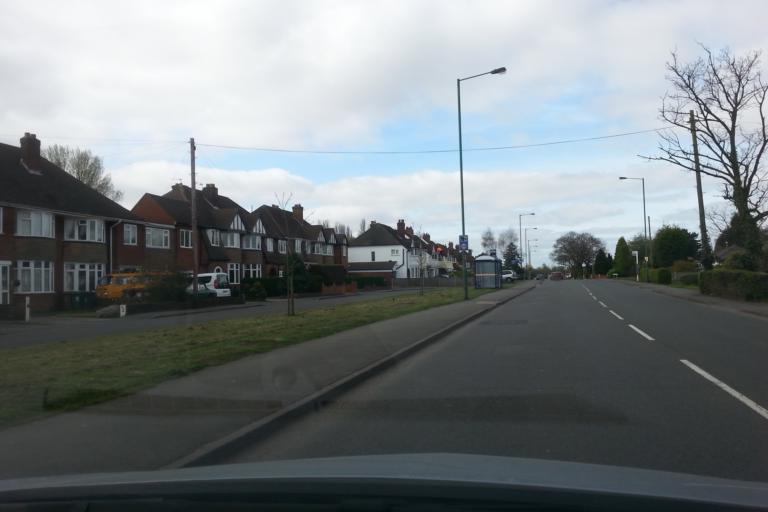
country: GB
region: England
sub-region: Walsall
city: Aldridge
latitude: 52.5979
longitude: -1.9286
